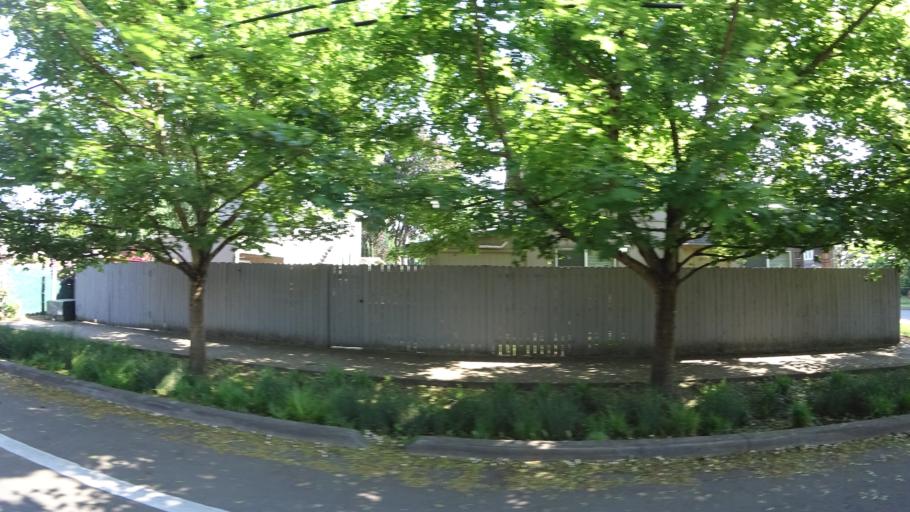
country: US
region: Oregon
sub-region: Multnomah County
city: Gresham
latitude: 45.5136
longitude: -122.4932
